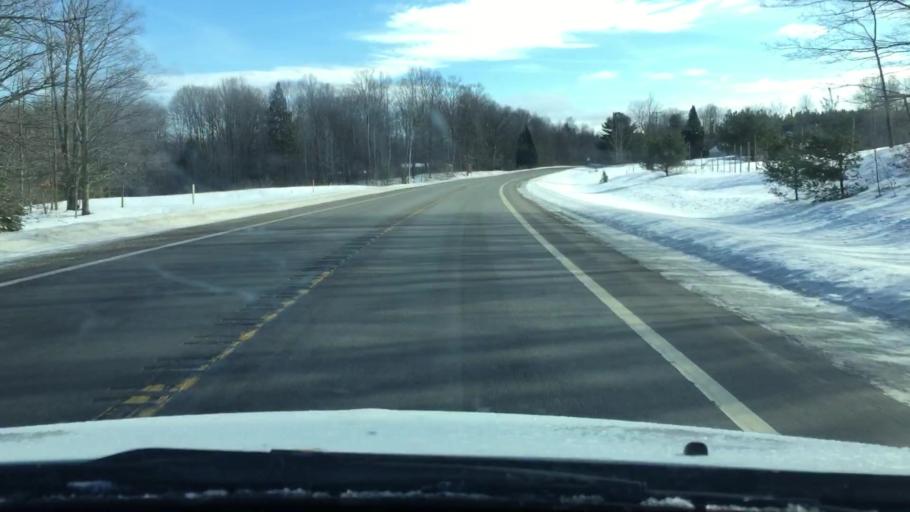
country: US
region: Michigan
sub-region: Antrim County
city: Mancelona
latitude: 44.9861
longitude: -85.0559
